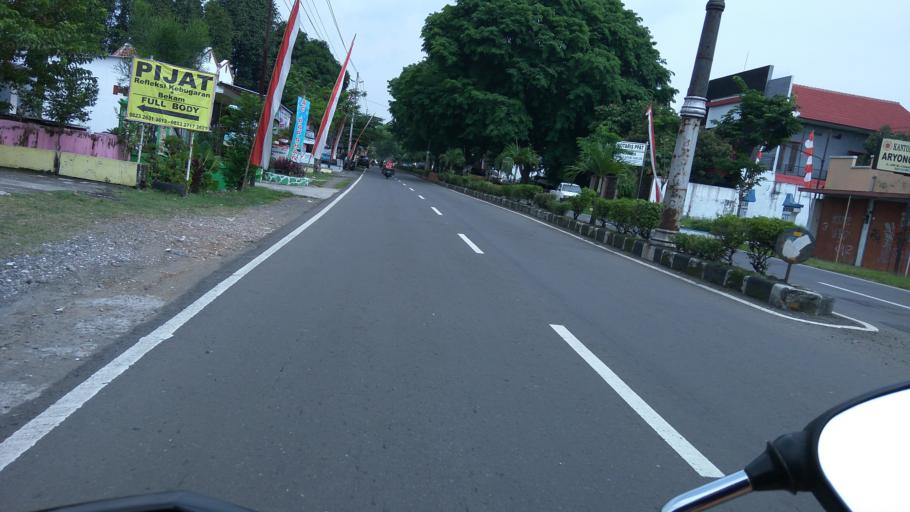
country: ID
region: Central Java
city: Jaten
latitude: -7.5881
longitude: 110.9226
